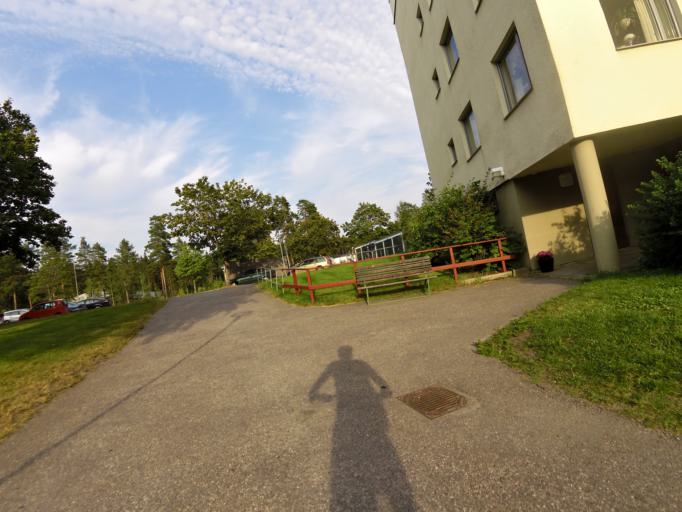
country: SE
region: Gaevleborg
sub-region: Gavle Kommun
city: Gavle
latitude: 60.6942
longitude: 17.1201
